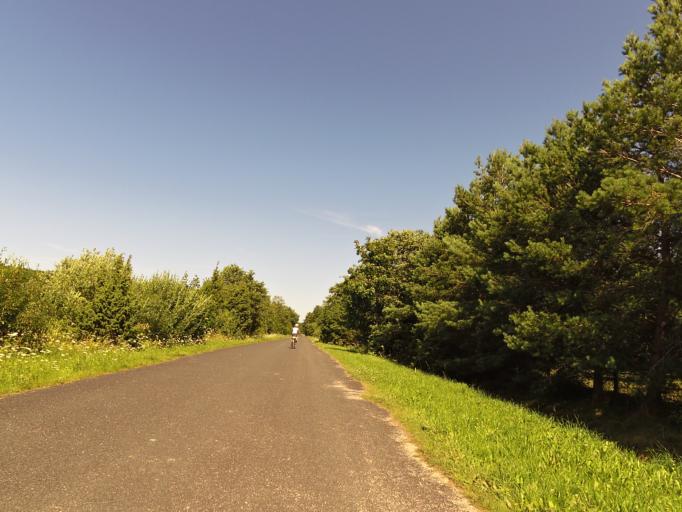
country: EE
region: Hiiumaa
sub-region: Kaerdla linn
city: Kardla
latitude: 58.7806
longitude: 22.4873
